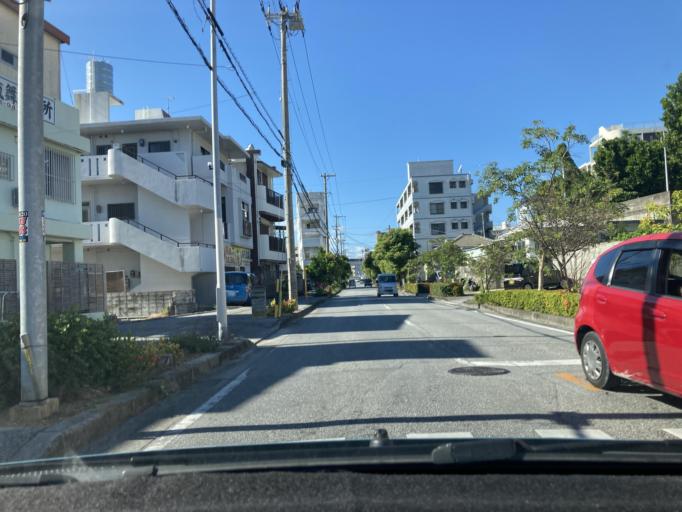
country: JP
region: Okinawa
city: Naha-shi
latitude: 26.2413
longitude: 127.6945
